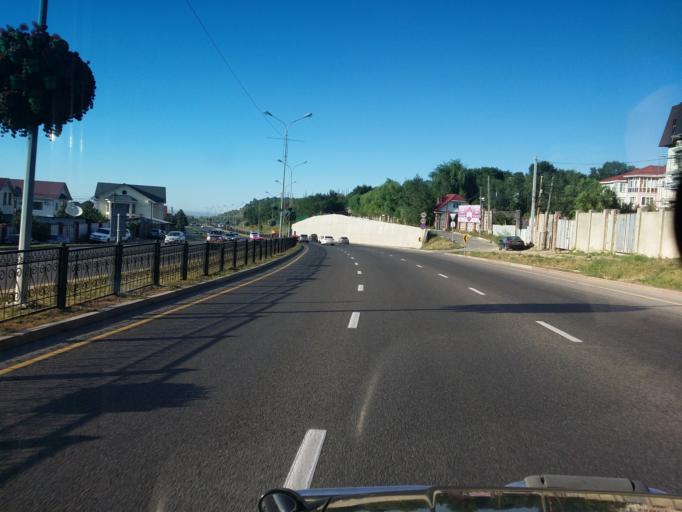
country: KZ
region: Almaty Qalasy
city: Almaty
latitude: 43.2490
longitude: 76.9809
